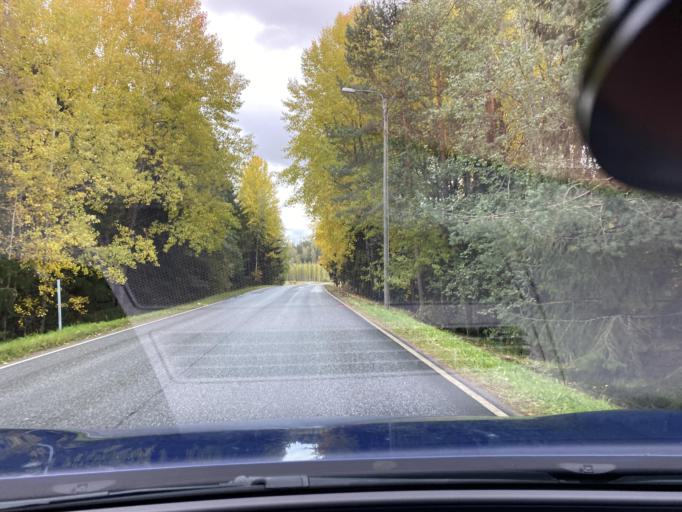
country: FI
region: Pirkanmaa
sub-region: Tampere
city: Nokia
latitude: 61.5018
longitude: 23.3419
